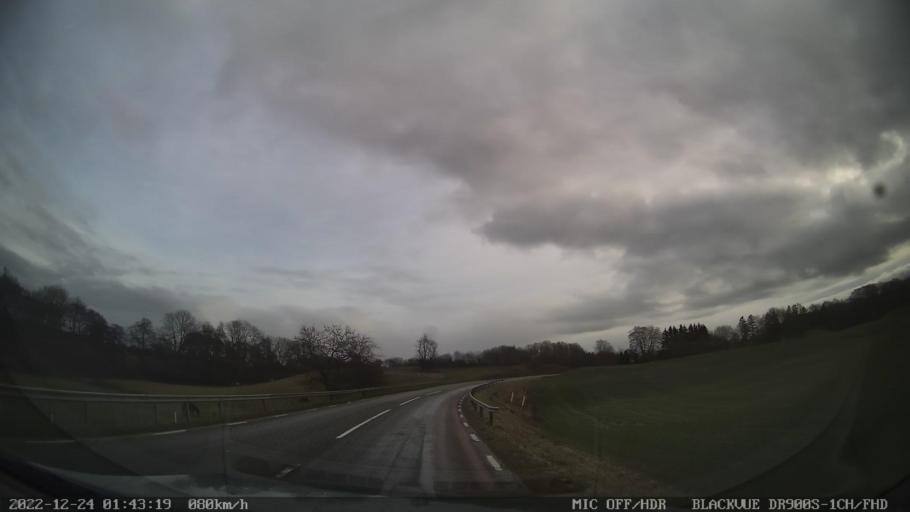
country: SE
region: Skane
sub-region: Tomelilla Kommun
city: Tomelilla
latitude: 55.5997
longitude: 14.0810
